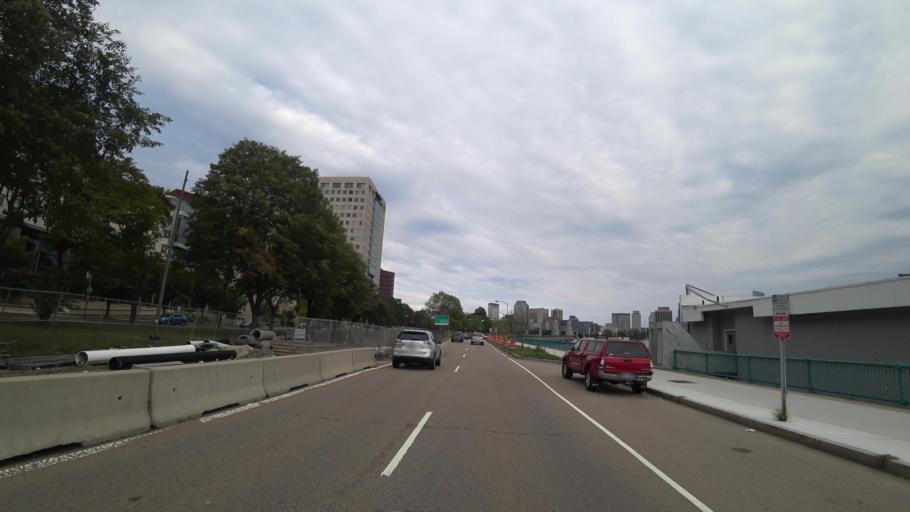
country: US
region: Massachusetts
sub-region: Suffolk County
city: Boston
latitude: 42.3602
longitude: -71.0832
